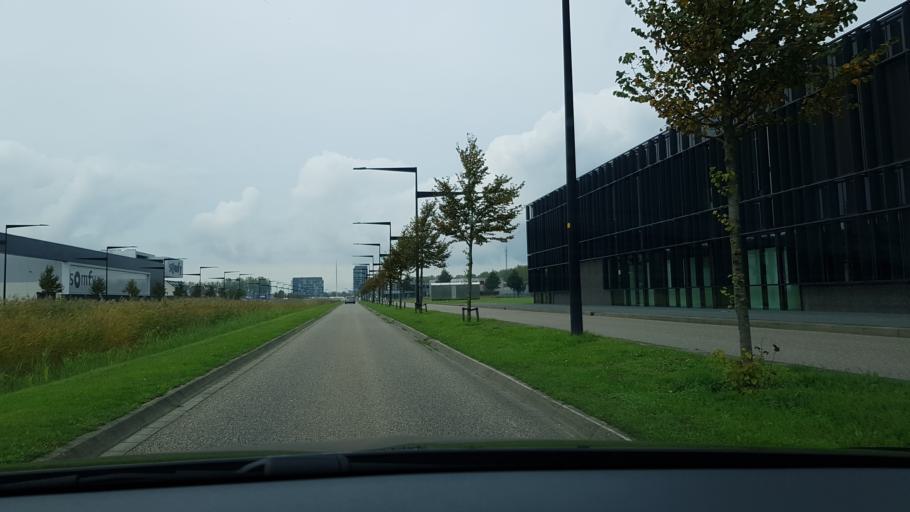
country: NL
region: North Holland
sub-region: Gemeente Haarlemmermeer
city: Hoofddorp
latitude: 52.2863
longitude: 4.6795
